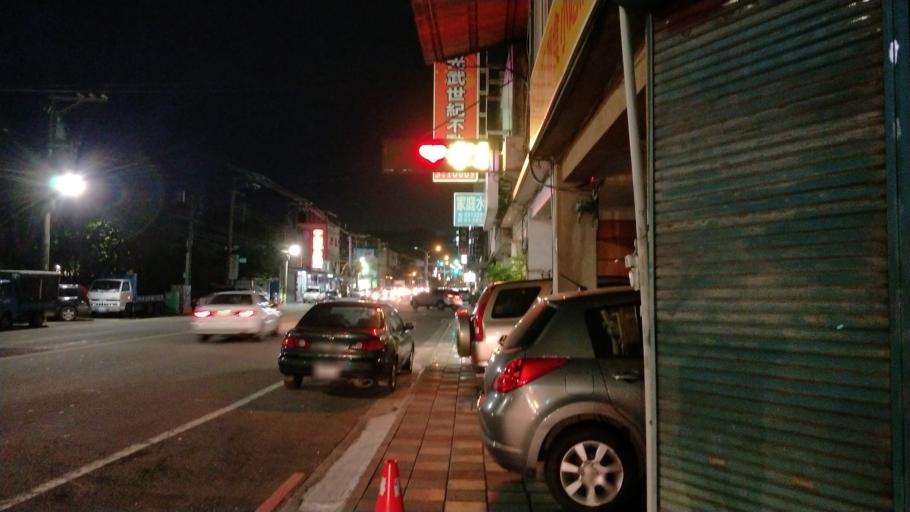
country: TW
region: Taiwan
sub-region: Hsinchu
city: Zhubei
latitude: 24.7302
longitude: 121.0928
